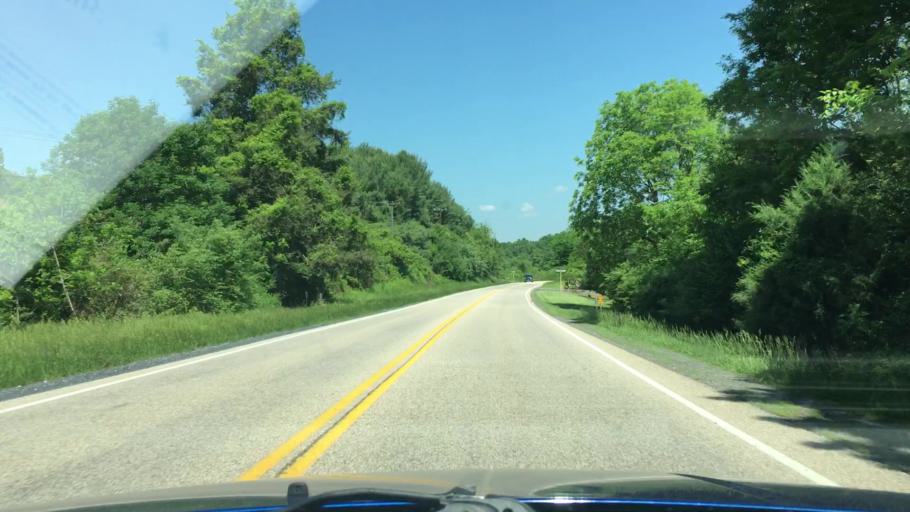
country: US
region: Virginia
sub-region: City of Staunton
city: Staunton
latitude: 38.1843
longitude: -79.1001
